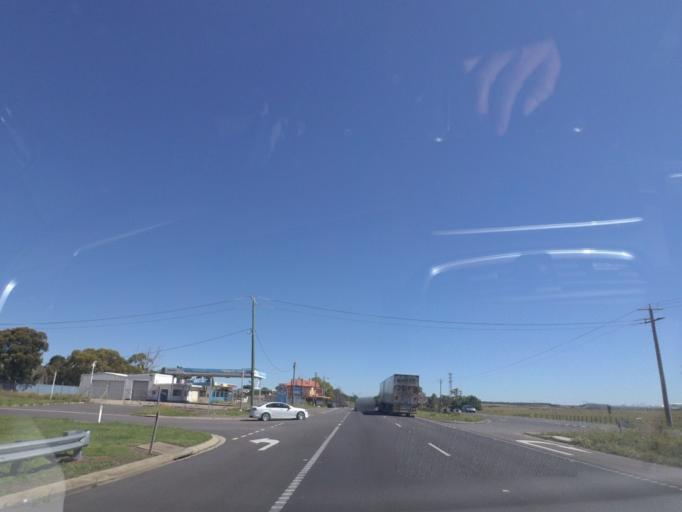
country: AU
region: Victoria
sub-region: Hume
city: Craigieburn
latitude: -37.5256
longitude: 144.9481
